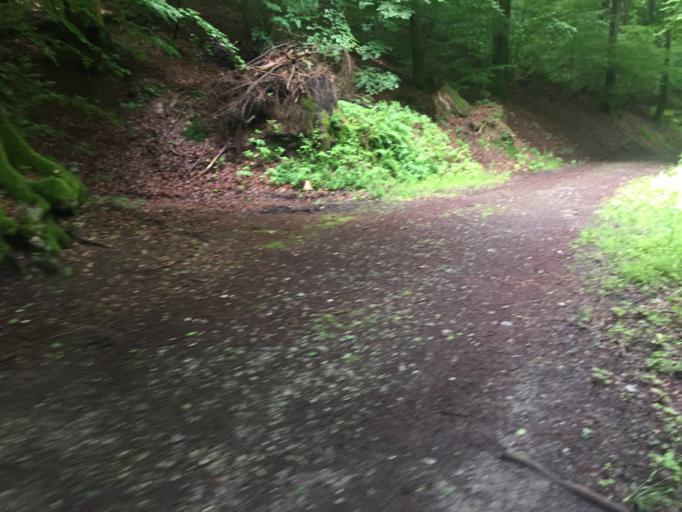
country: CH
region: Bern
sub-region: Bern-Mittelland District
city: Koniz
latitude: 46.9331
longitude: 7.3974
